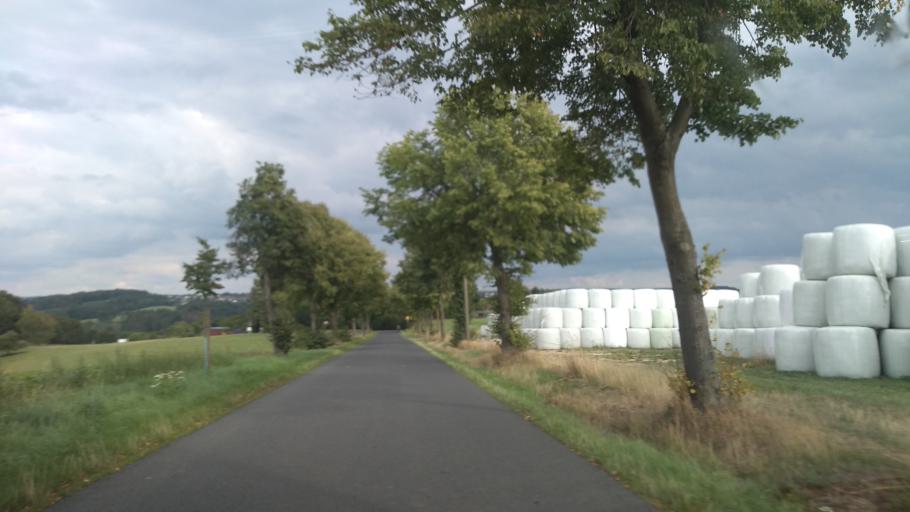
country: DE
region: North Rhine-Westphalia
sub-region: Regierungsbezirk Koln
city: Hennef
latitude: 50.8513
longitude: 7.3053
